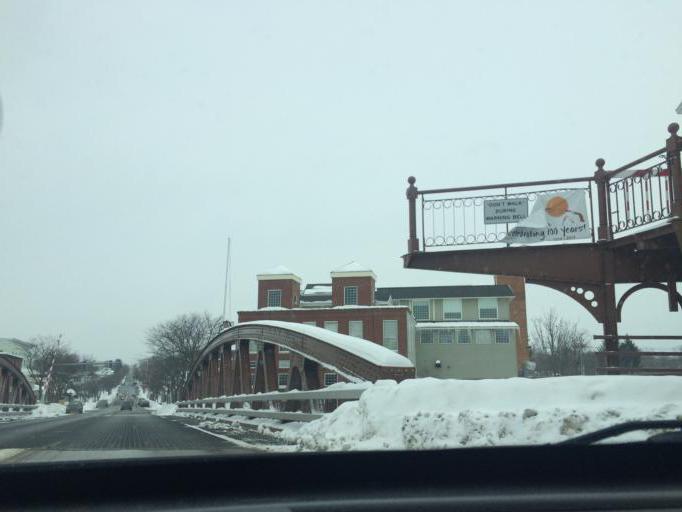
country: US
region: New York
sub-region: Monroe County
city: Fairport
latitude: 43.1011
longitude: -77.4419
